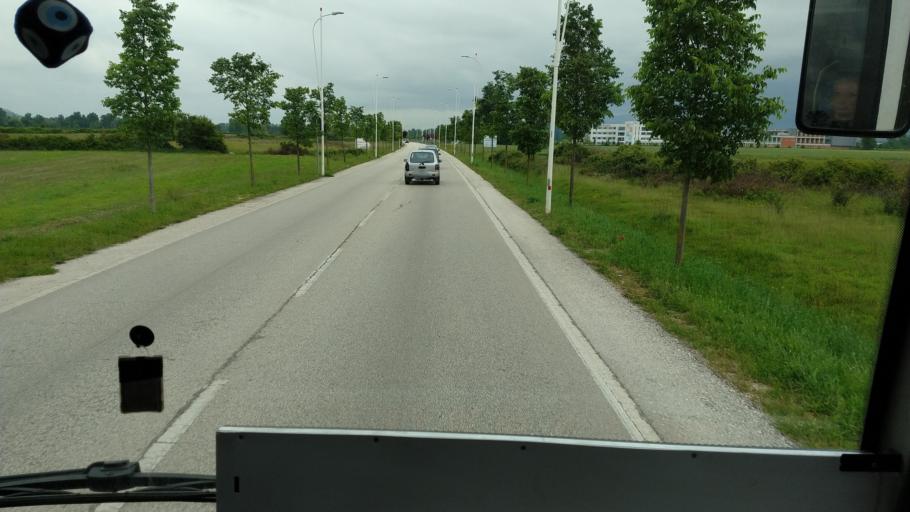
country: AL
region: Tirane
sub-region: Rrethi i Tiranes
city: Berxull
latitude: 41.4000
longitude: 19.7043
